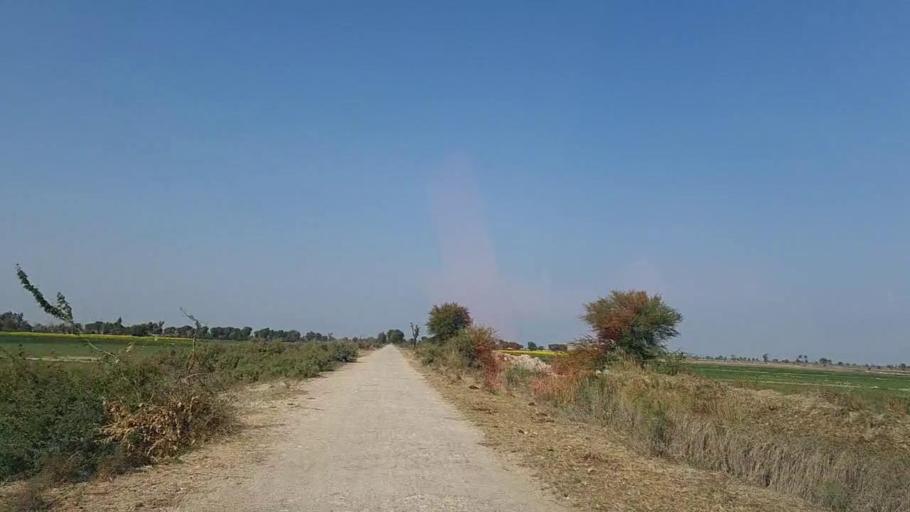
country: PK
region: Sindh
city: Sanghar
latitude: 26.0105
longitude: 69.0537
